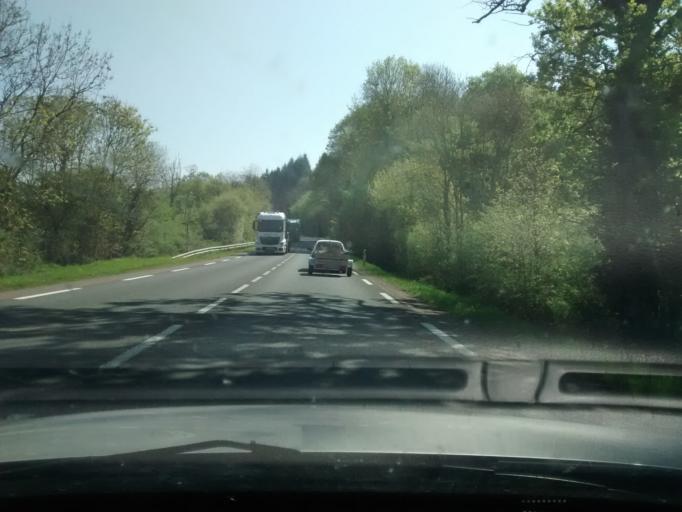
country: FR
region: Pays de la Loire
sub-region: Departement de la Sarthe
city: Brulon
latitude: 48.0270
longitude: -0.2566
